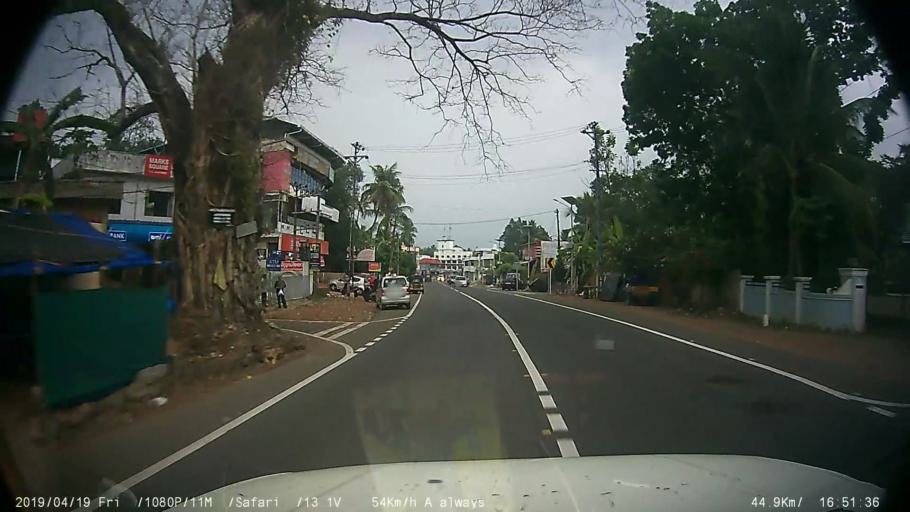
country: IN
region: Kerala
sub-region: Kottayam
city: Changanacheri
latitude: 9.4561
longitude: 76.5341
